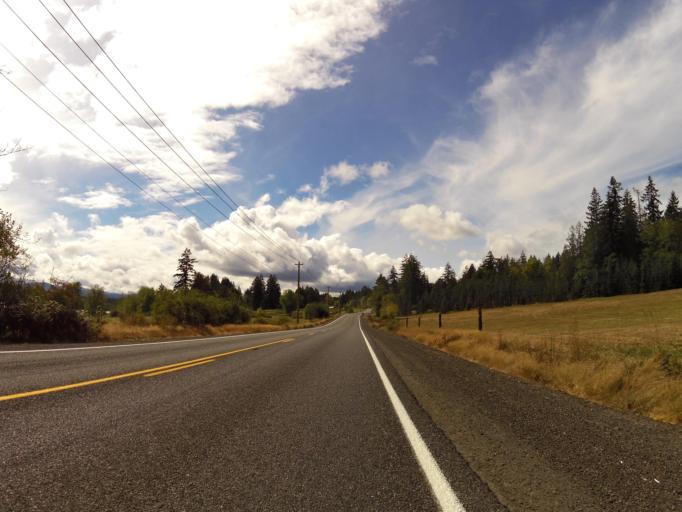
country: US
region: Washington
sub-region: Mason County
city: Shelton
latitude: 47.1551
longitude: -123.0546
